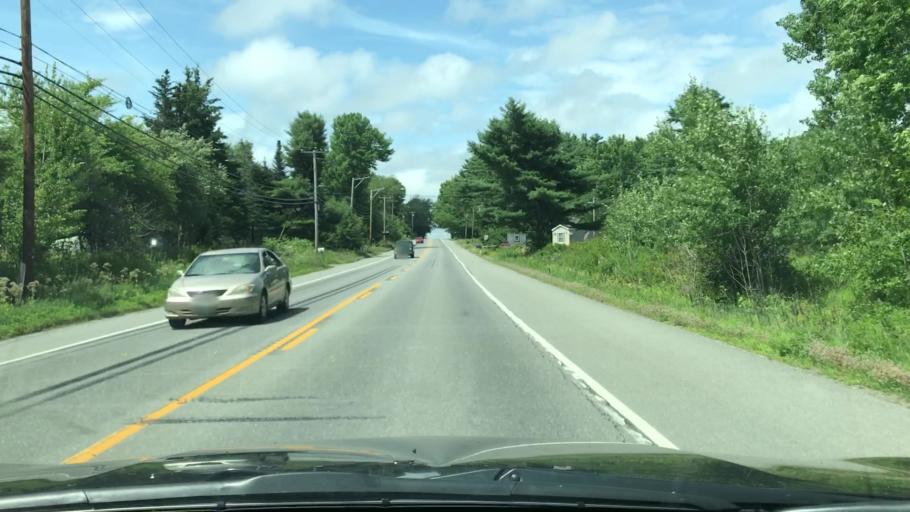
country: US
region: Maine
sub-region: Waldo County
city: Belfast
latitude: 44.3853
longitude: -68.9875
